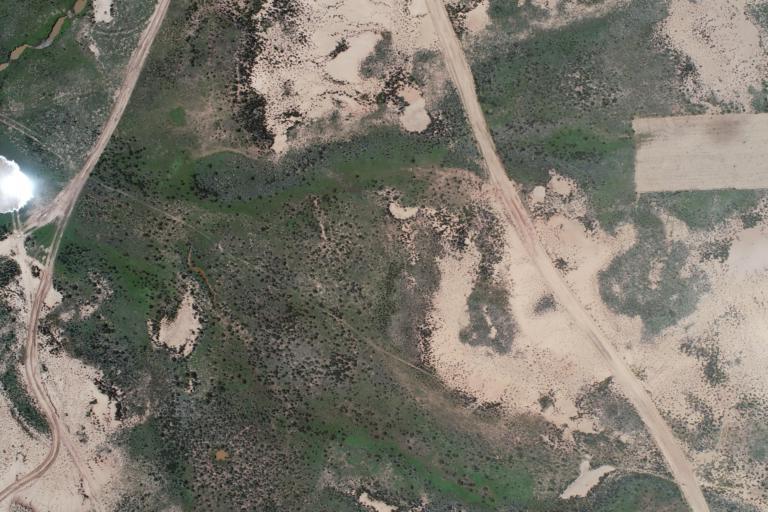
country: BO
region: La Paz
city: Curahuara de Carangas
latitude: -17.2940
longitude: -68.4970
